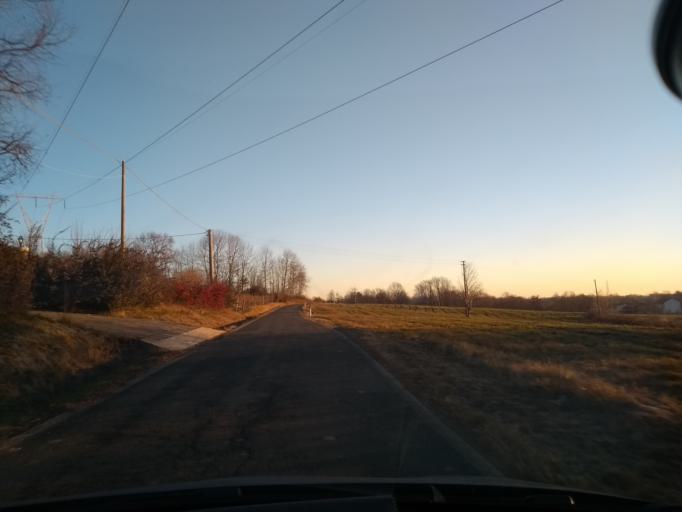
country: IT
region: Piedmont
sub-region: Provincia di Torino
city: Balangero
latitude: 45.2790
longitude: 7.5408
